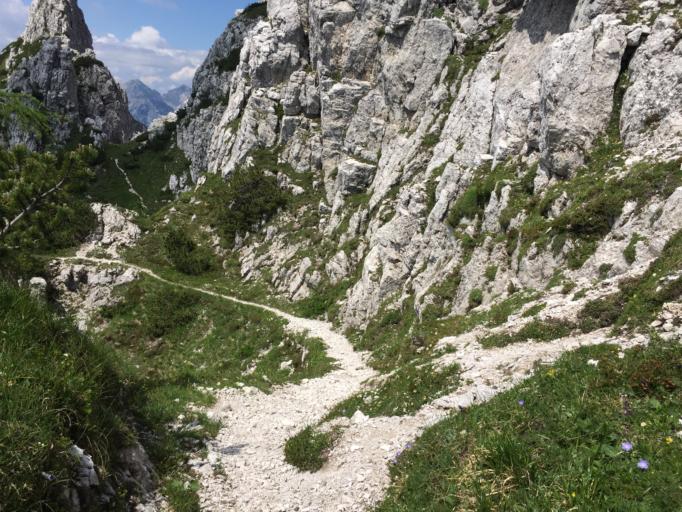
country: IT
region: Friuli Venezia Giulia
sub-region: Provincia di Udine
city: Pontebba
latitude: 46.4706
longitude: 13.2447
